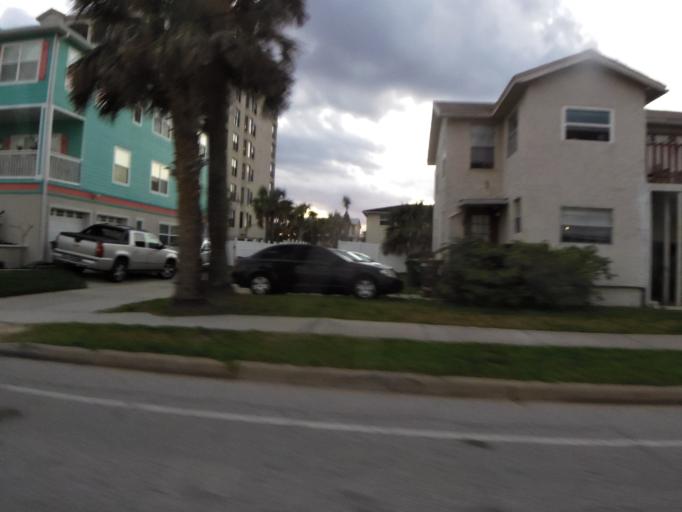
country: US
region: Florida
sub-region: Duval County
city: Jacksonville Beach
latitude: 30.2806
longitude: -81.3879
